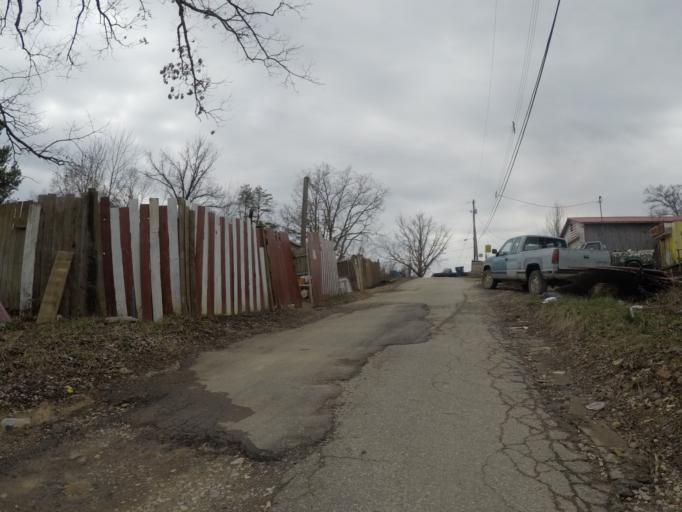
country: US
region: West Virginia
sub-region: Cabell County
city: Huntington
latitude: 38.3911
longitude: -82.3847
